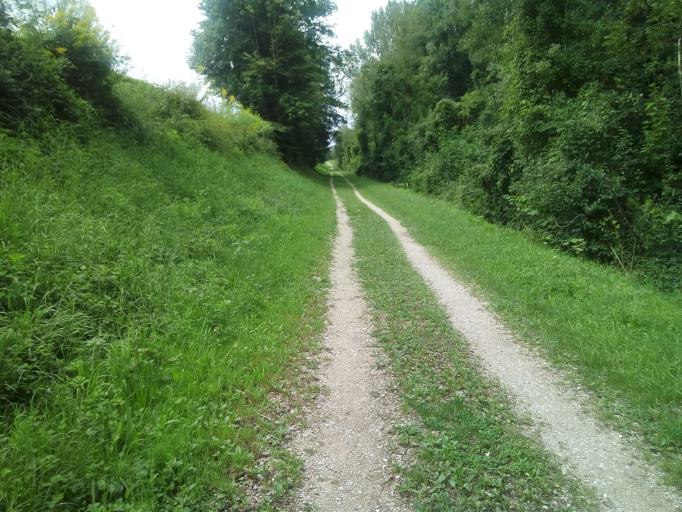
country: DE
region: Bavaria
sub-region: Upper Bavaria
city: Unterfoehring
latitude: 48.1988
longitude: 11.6414
